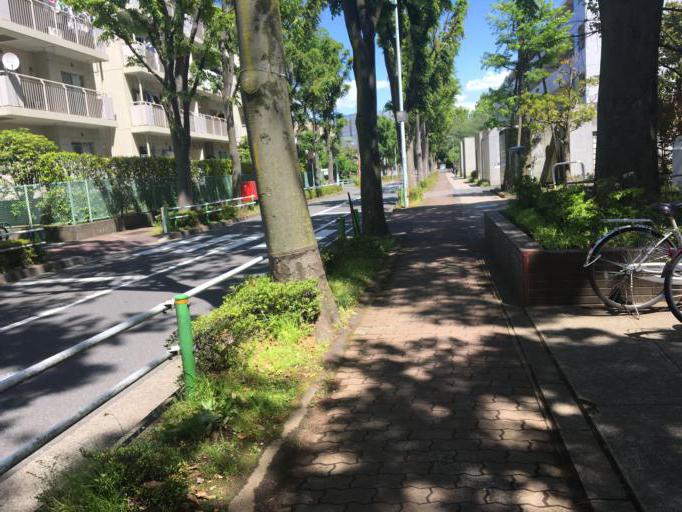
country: JP
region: Saitama
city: Wako
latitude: 35.7700
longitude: 139.6394
